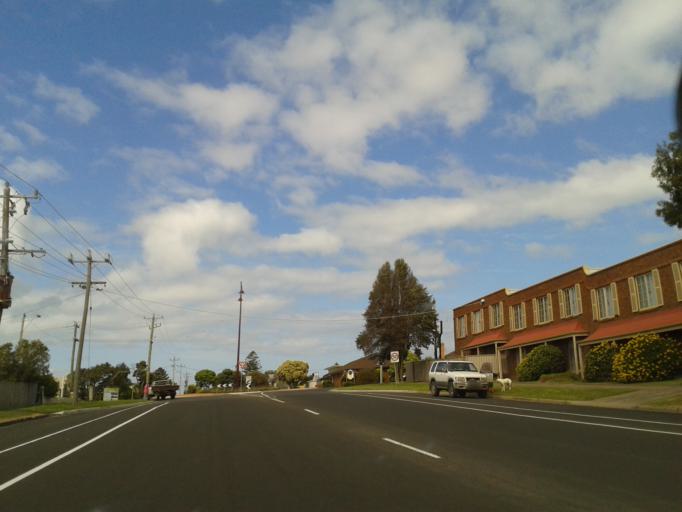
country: AU
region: Victoria
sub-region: Glenelg
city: Portland
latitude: -38.3421
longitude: 141.6030
